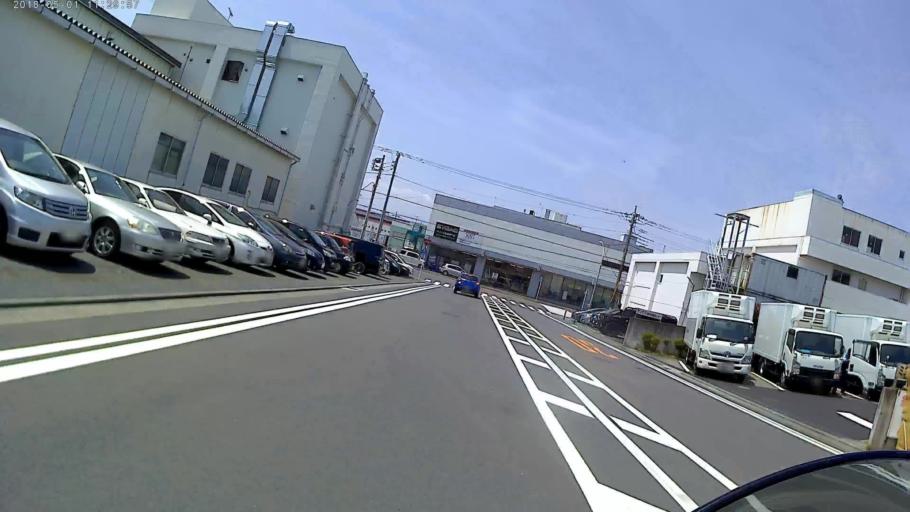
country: JP
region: Kanagawa
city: Minami-rinkan
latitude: 35.5004
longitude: 139.4866
